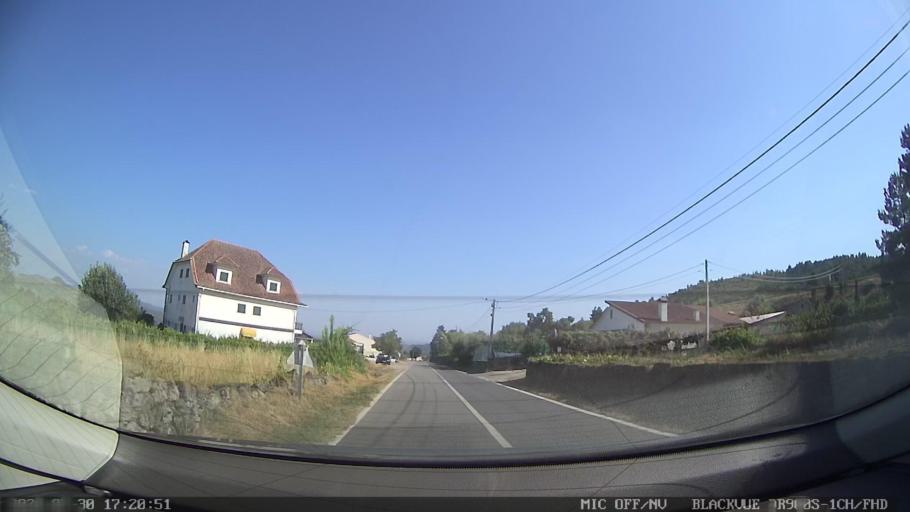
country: PT
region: Vila Real
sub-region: Sabrosa
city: Sabrosa
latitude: 41.2942
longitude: -7.4807
